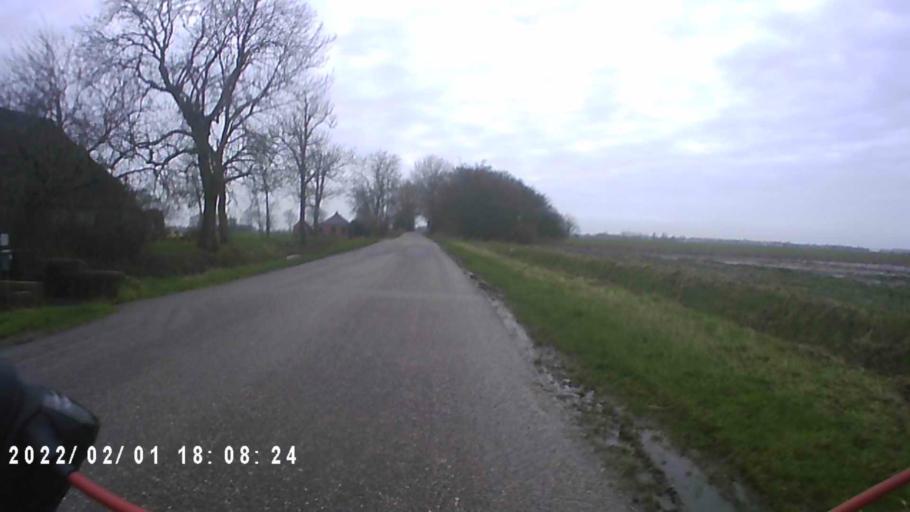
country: NL
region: Groningen
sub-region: Gemeente De Marne
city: Ulrum
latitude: 53.3428
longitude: 6.3585
